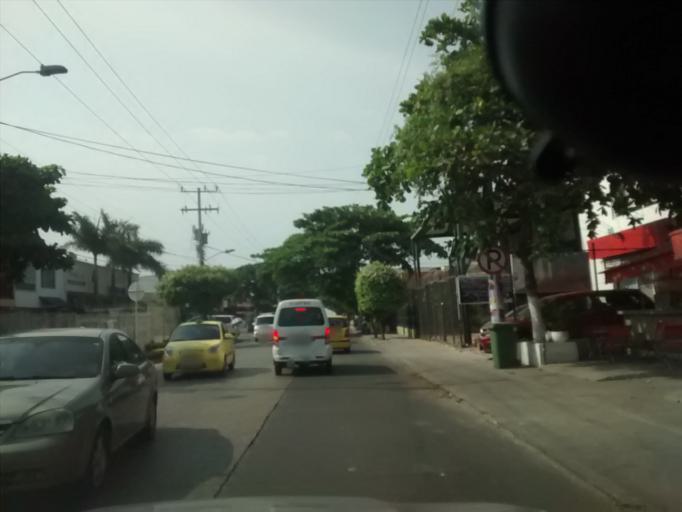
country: CO
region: Bolivar
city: Cartagena
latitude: 10.4475
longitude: -75.5174
